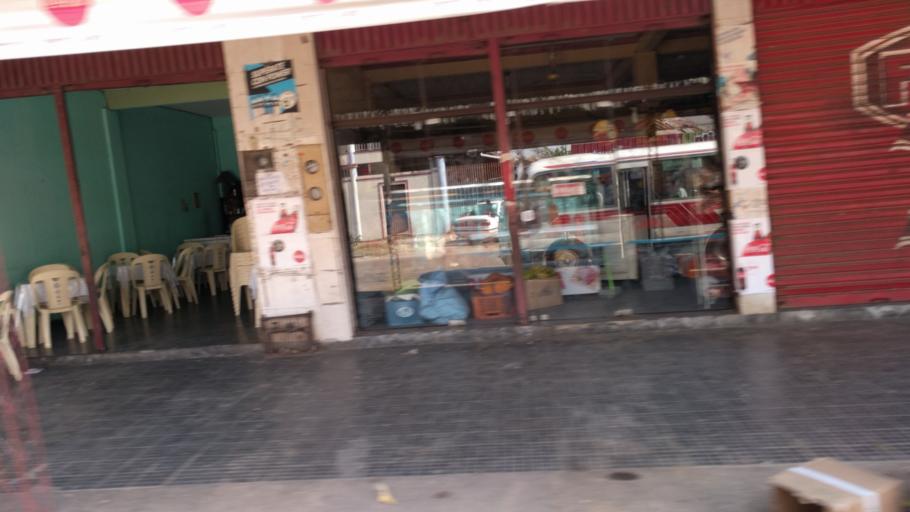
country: BO
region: Santa Cruz
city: Santa Cruz de la Sierra
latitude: -17.8223
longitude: -63.1697
